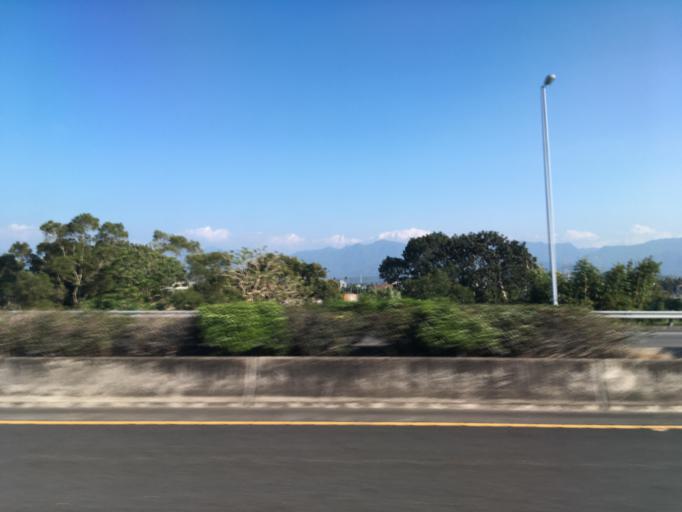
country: TW
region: Taiwan
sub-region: Chiayi
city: Jiayi Shi
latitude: 23.4448
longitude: 120.4821
